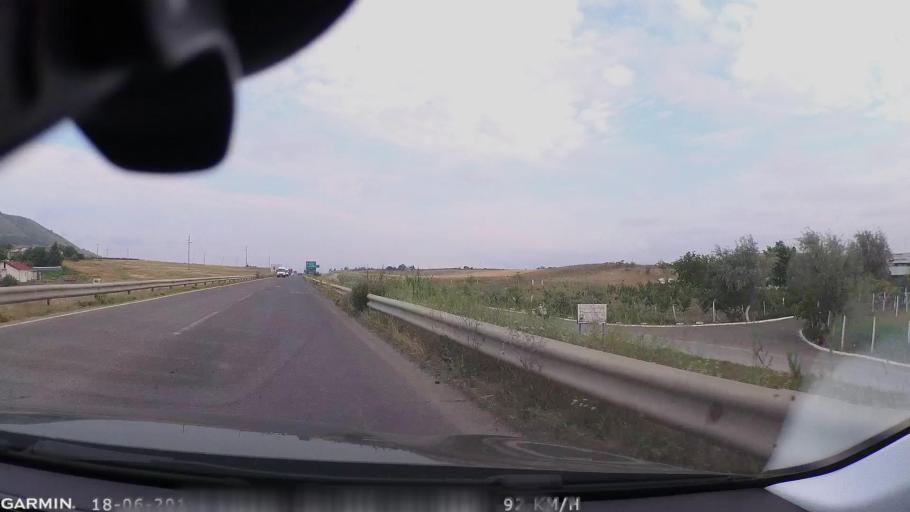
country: MK
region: Stip
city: Shtip
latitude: 41.7764
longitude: 22.1345
